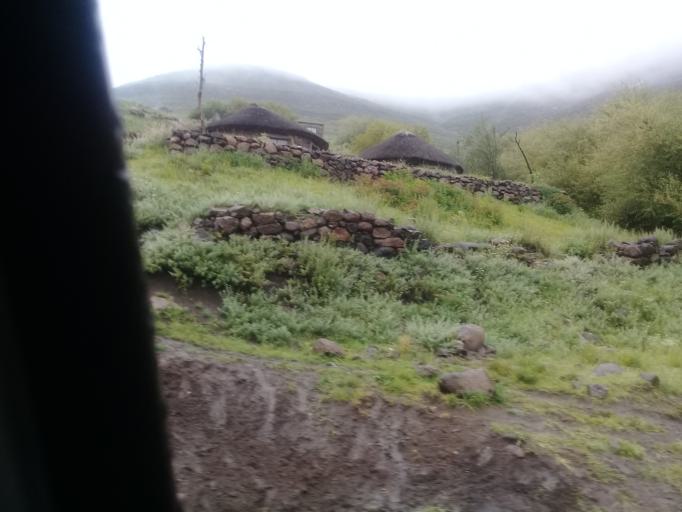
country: LS
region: Mokhotlong
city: Mokhotlong
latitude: -29.3904
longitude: 28.9639
